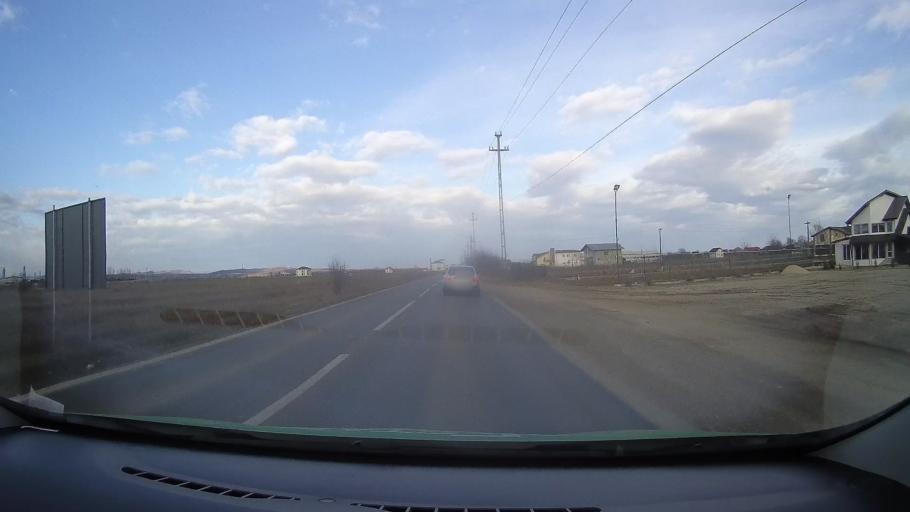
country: RO
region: Dambovita
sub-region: Comuna Ulmi
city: Ulmi
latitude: 44.8958
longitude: 25.5114
